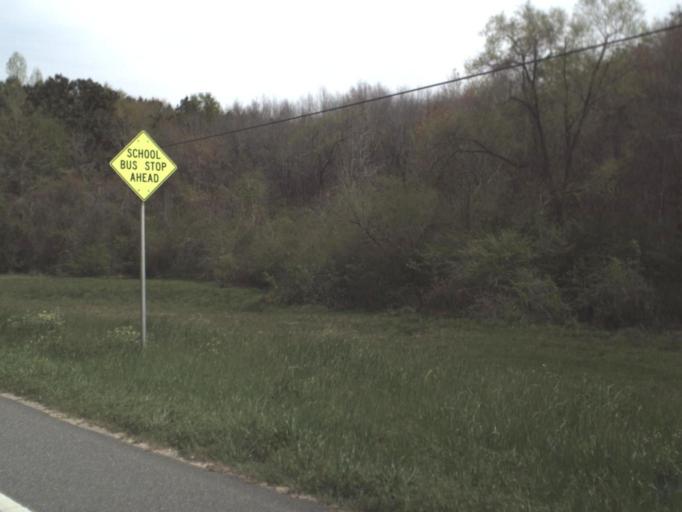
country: US
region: Florida
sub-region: Jackson County
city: Graceville
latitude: 30.9718
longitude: -85.6386
